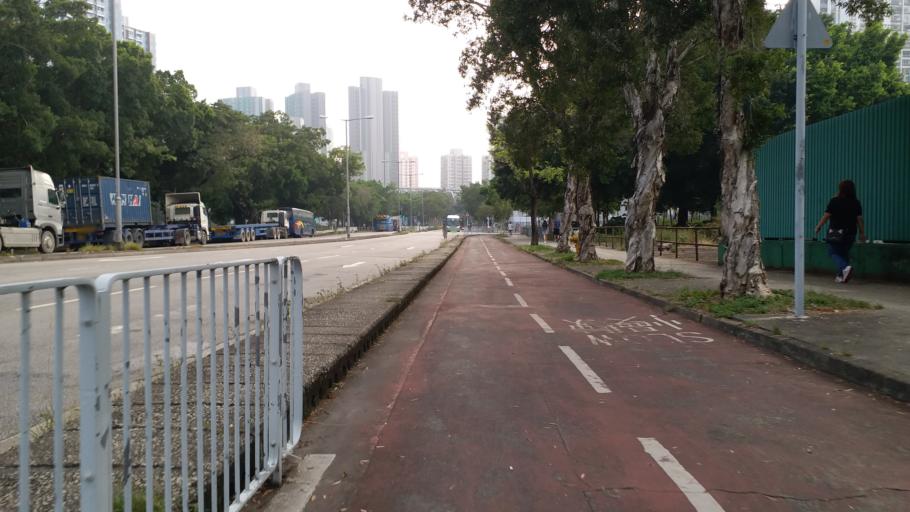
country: HK
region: Yuen Long
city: Yuen Long Kau Hui
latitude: 22.4517
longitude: 114.0271
